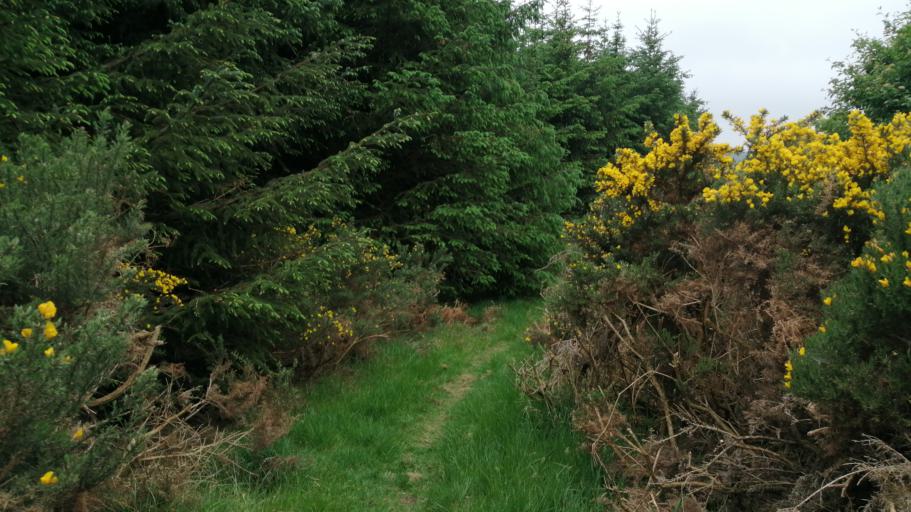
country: GB
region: Scotland
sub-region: Moray
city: Cullen
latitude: 57.5795
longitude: -2.7812
